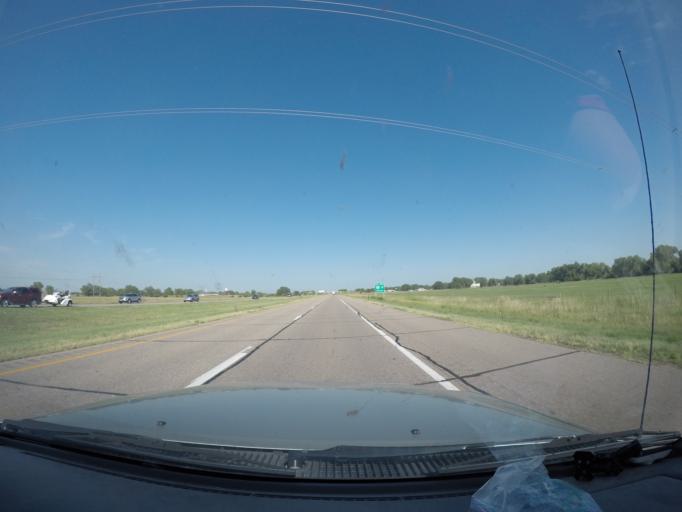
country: US
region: Nebraska
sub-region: Buffalo County
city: Kearney
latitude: 40.6767
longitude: -99.2656
